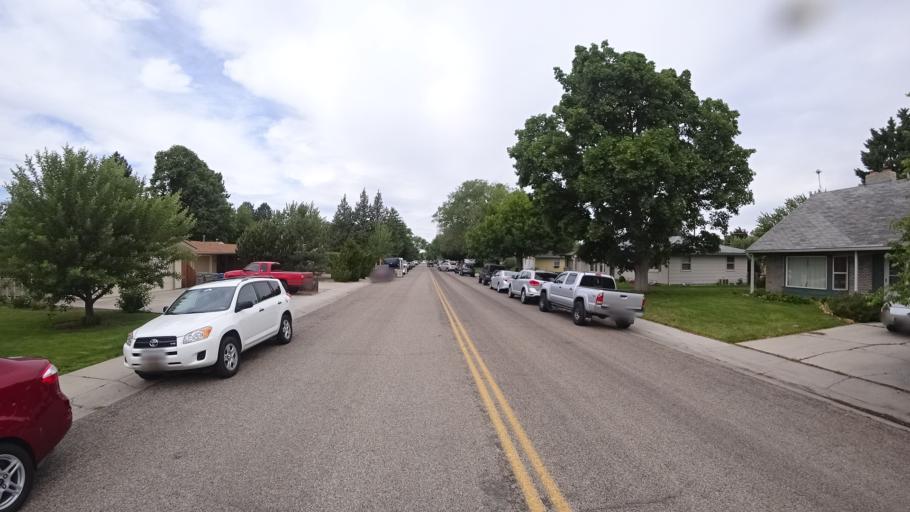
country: US
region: Idaho
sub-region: Ada County
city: Boise
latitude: 43.5771
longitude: -116.2056
